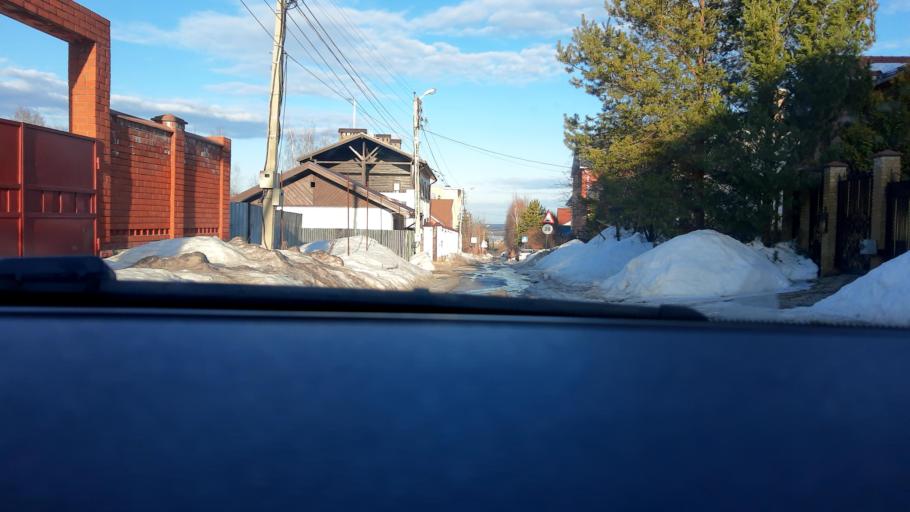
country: RU
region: Nizjnij Novgorod
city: Afonino
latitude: 56.2855
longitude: 44.0906
